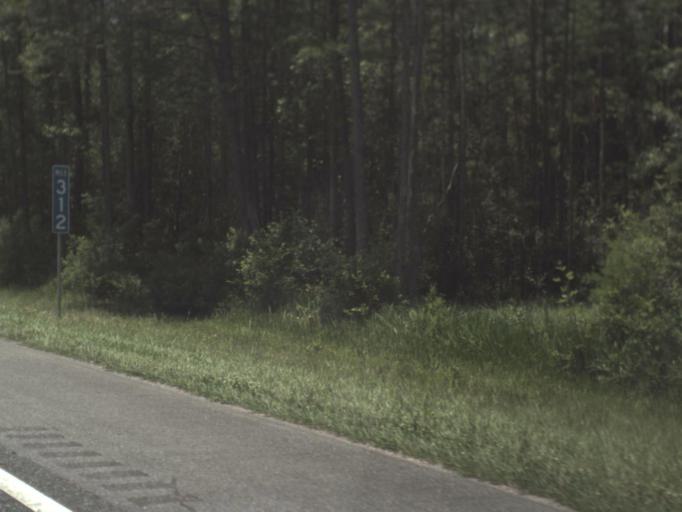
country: US
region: Florida
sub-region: Columbia County
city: Watertown
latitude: 30.2547
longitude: -82.4980
